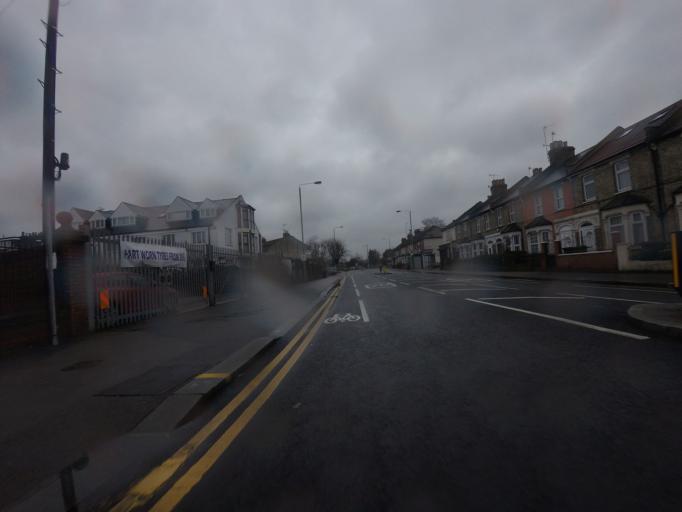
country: GB
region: England
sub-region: Greater London
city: Walthamstow
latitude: 51.5937
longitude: -0.0181
